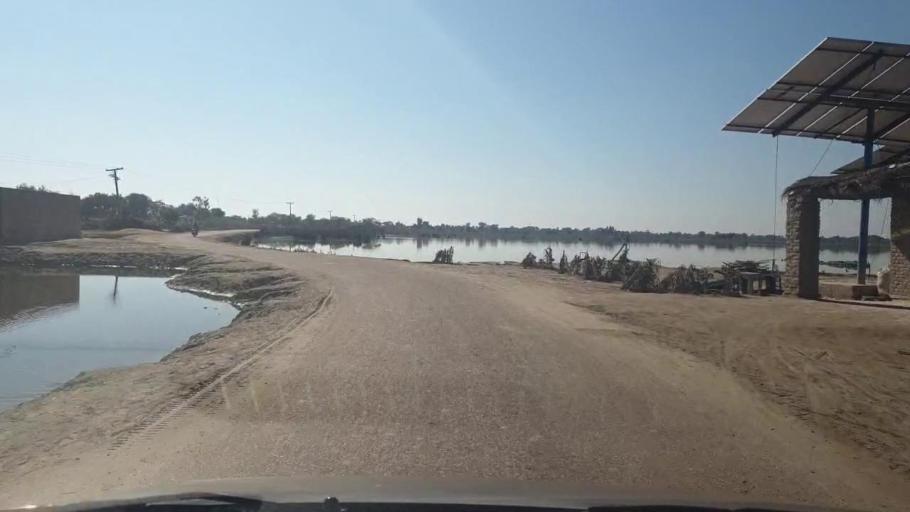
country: PK
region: Sindh
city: Bozdar
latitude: 27.1337
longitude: 68.6418
